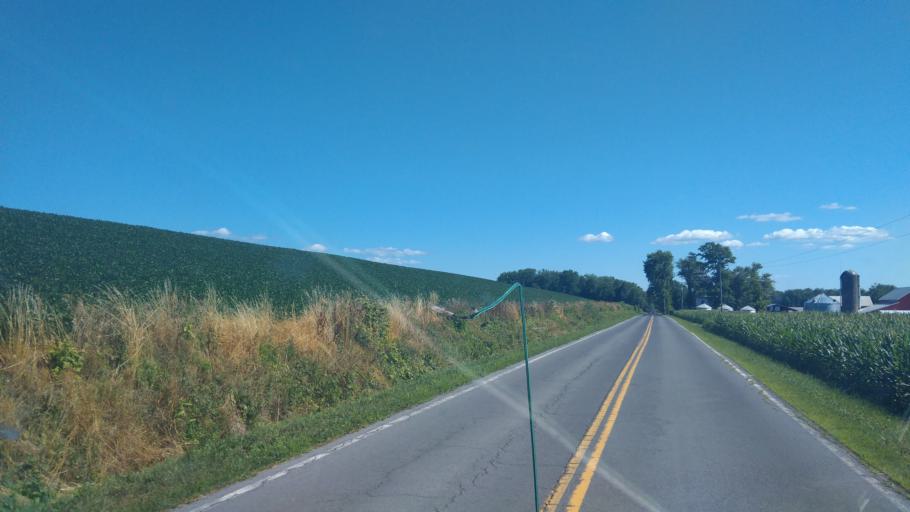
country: US
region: New York
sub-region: Wayne County
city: Clyde
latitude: 43.0169
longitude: -76.8122
